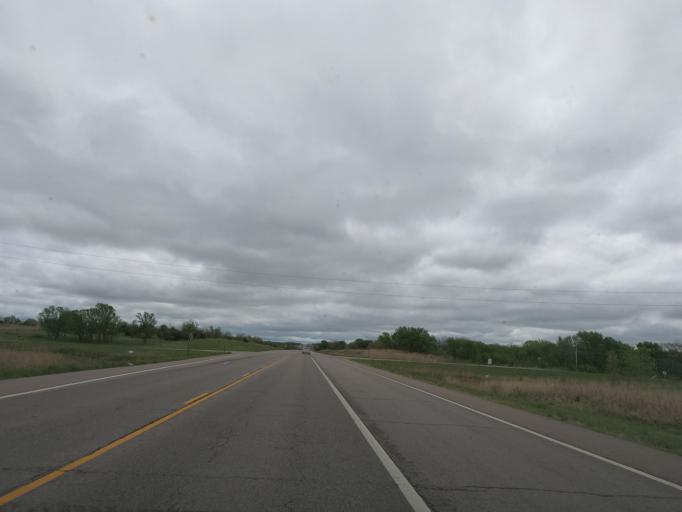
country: US
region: Kansas
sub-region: Elk County
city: Howard
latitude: 37.6364
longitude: -96.3680
